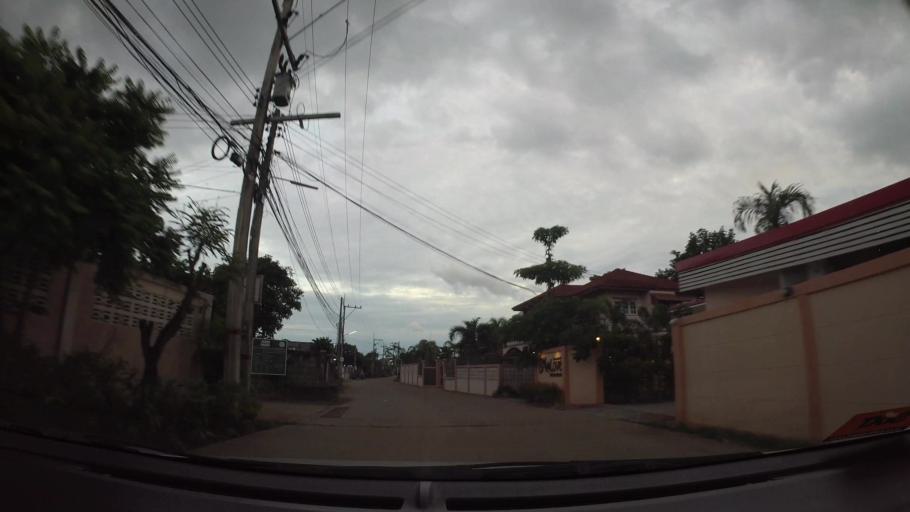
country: TH
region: Chon Buri
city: Sattahip
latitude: 12.6964
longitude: 100.8948
